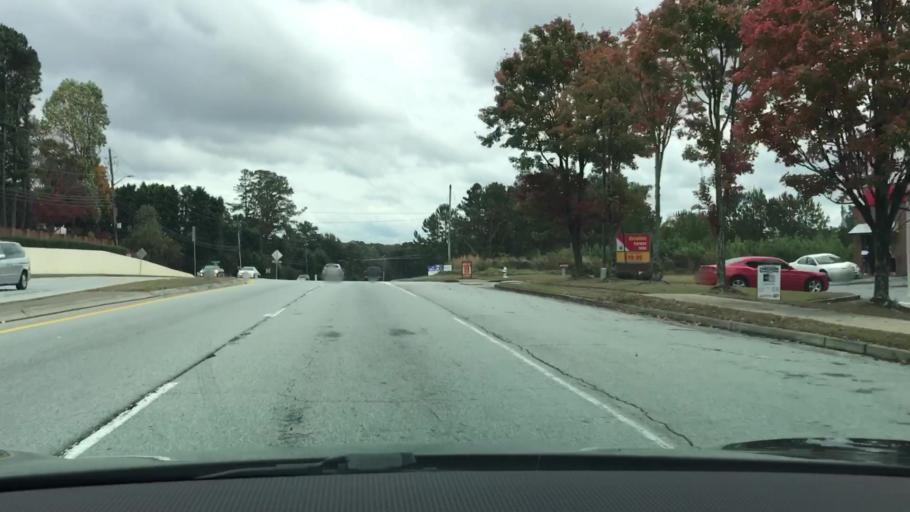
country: US
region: Georgia
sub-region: Gwinnett County
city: Lawrenceville
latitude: 33.9841
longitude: -84.0228
